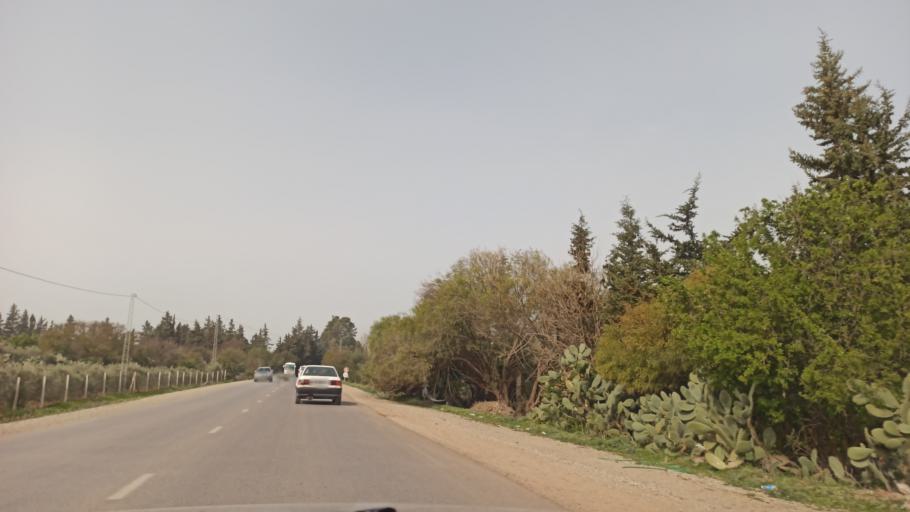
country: TN
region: Zaghwan
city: Zaghouan
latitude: 36.4216
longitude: 10.0975
